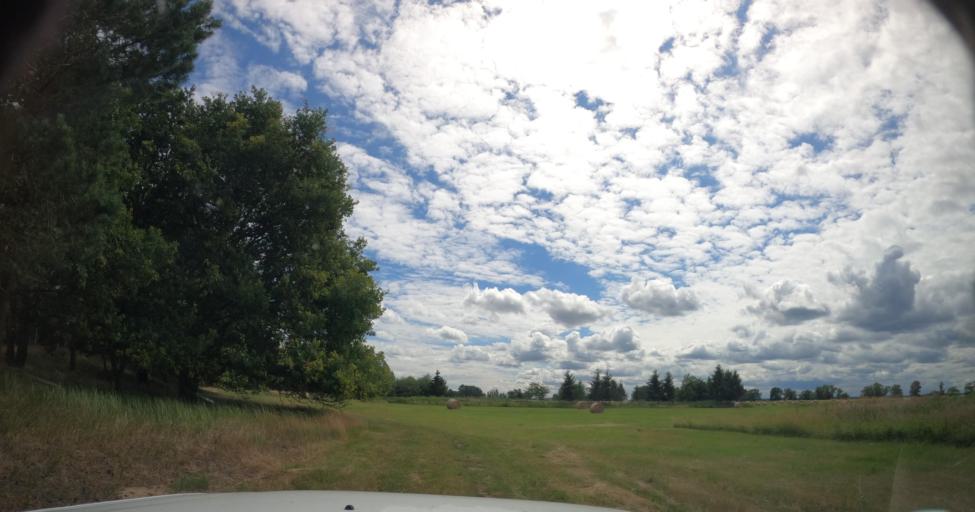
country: PL
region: West Pomeranian Voivodeship
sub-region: Powiat goleniowski
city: Stepnica
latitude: 53.7072
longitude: 14.5458
